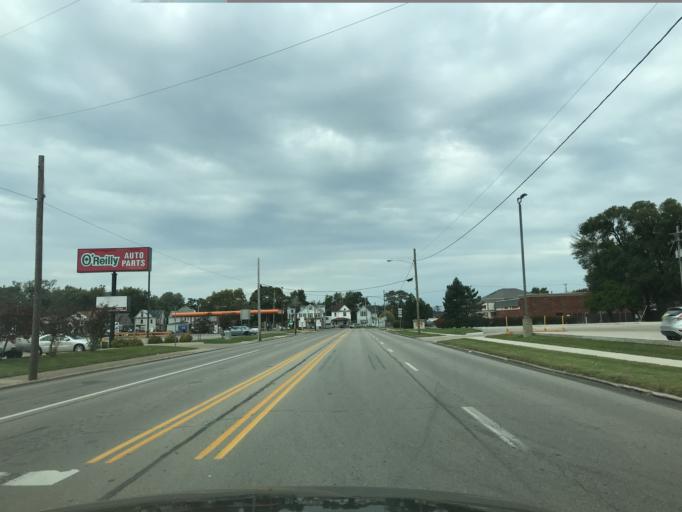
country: US
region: Pennsylvania
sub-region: Erie County
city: Wesleyville
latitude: 42.1266
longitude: -80.0437
